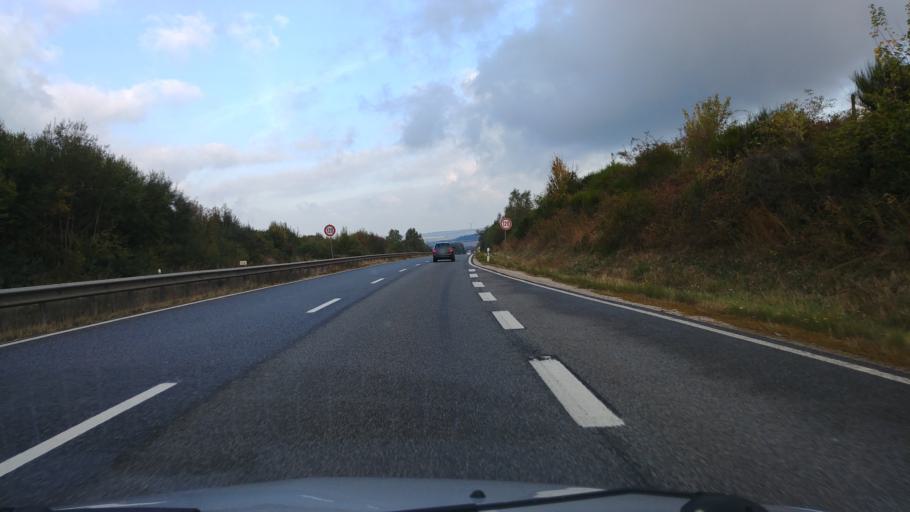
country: DE
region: Rheinland-Pfalz
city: Riesweiler
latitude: 49.9697
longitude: 7.5616
